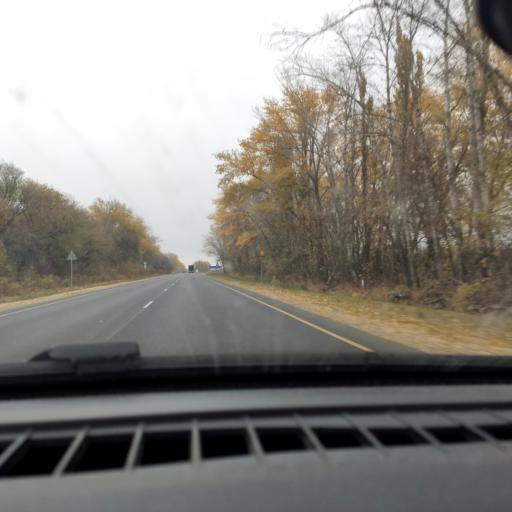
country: RU
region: Voronezj
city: Uryv-Pokrovka
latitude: 51.1671
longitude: 39.0726
